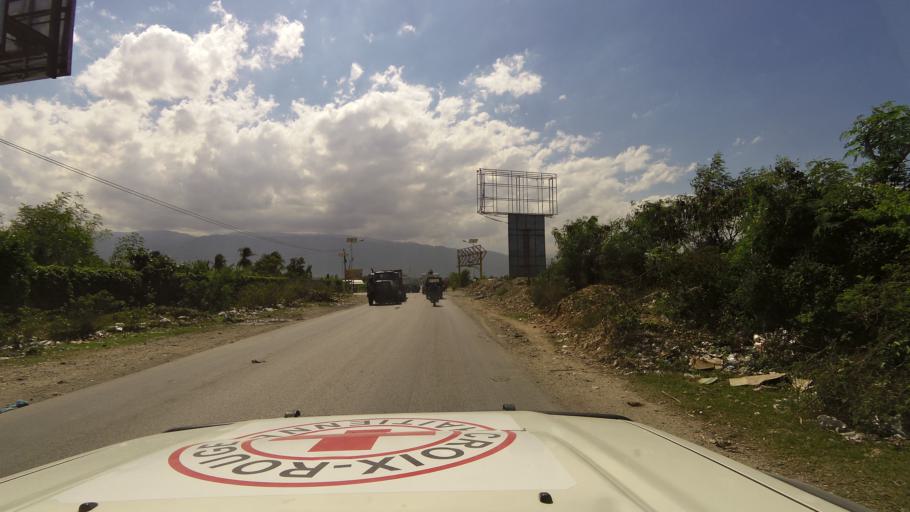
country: HT
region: Ouest
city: Delmas 73
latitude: 18.5910
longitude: -72.3258
